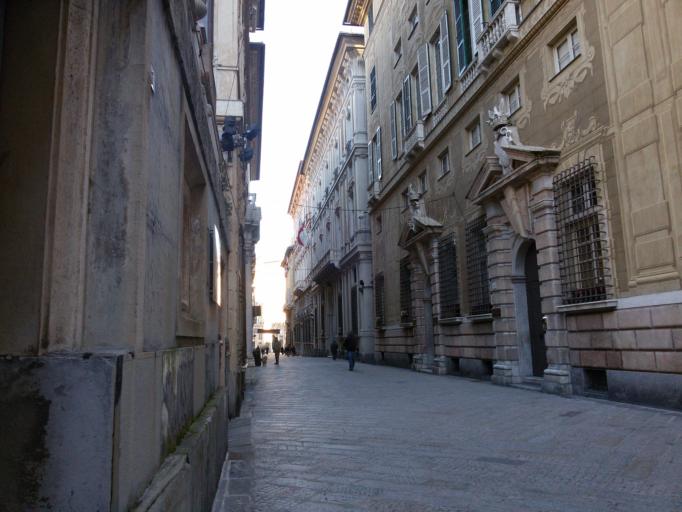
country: IT
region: Liguria
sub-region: Provincia di Genova
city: San Teodoro
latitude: 44.4111
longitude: 8.9331
